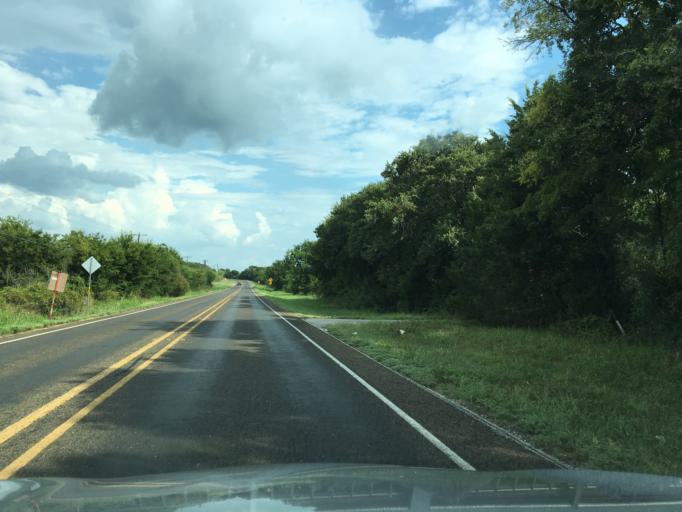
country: US
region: Texas
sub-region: Denton County
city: Corinth
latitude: 33.2003
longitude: -97.0634
